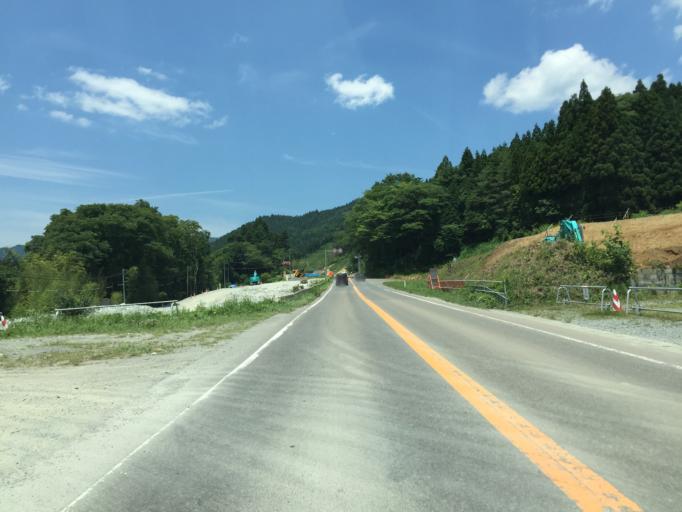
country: JP
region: Miyagi
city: Marumori
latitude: 37.7699
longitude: 140.8448
